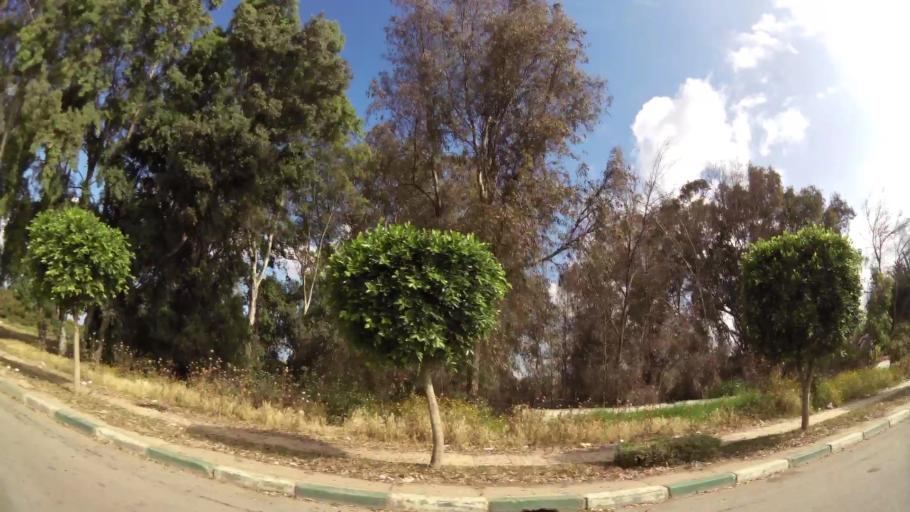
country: MA
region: Gharb-Chrarda-Beni Hssen
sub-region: Kenitra Province
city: Kenitra
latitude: 34.2775
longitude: -6.5504
